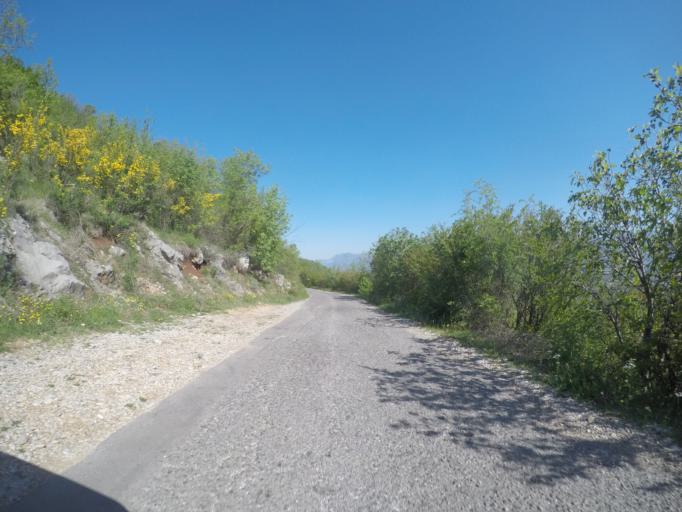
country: ME
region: Danilovgrad
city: Danilovgrad
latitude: 42.5163
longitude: 19.0982
